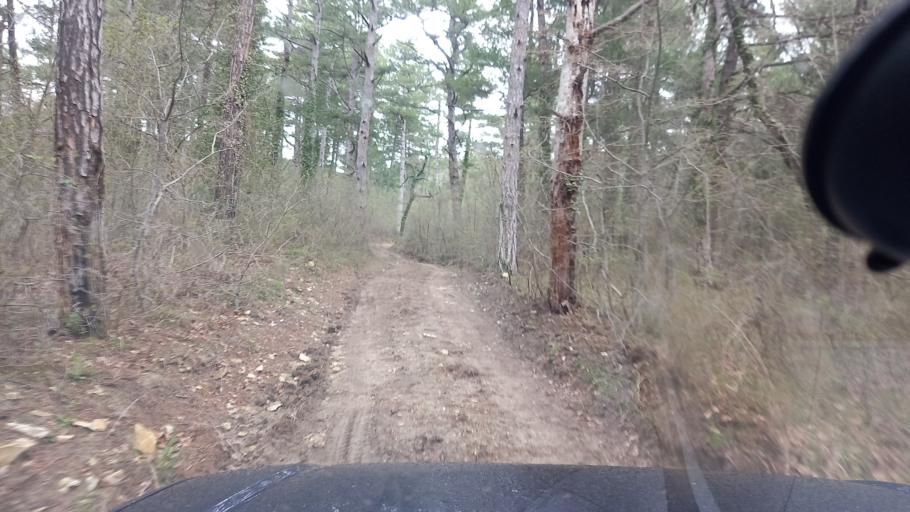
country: RU
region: Krasnodarskiy
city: Arkhipo-Osipovka
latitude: 44.3703
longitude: 38.4725
